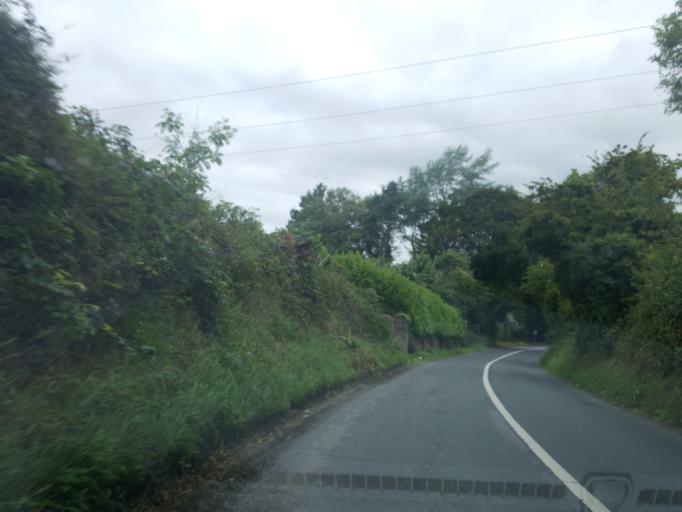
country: IE
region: Leinster
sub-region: Wicklow
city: Valleymount
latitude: 53.1307
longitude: -6.6045
